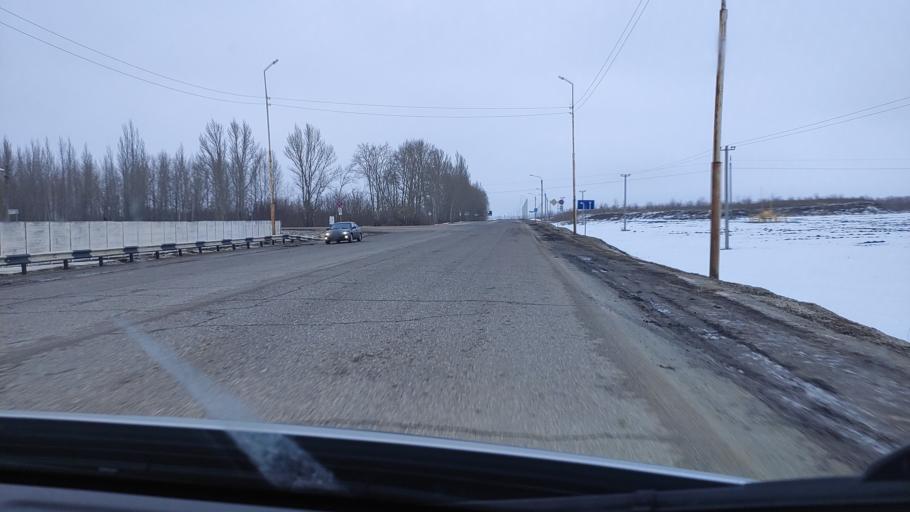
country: RU
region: Tambov
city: Mordovo
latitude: 52.0912
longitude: 40.8062
